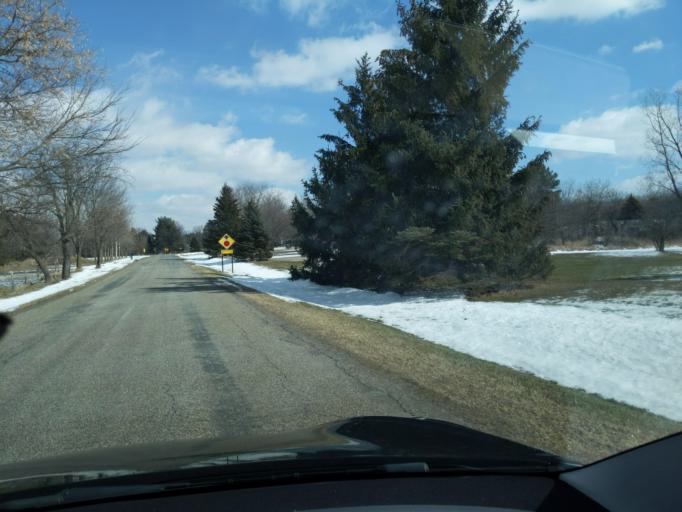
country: US
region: Michigan
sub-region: Ingham County
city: Mason
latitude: 42.6124
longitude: -84.3606
